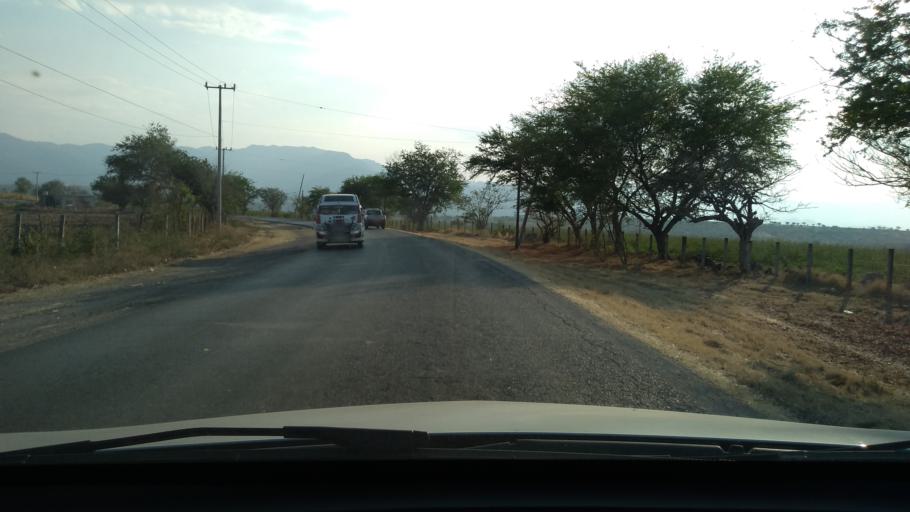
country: MX
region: Morelos
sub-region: Jojutla
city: Tehuixtla
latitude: 18.5865
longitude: -99.2629
